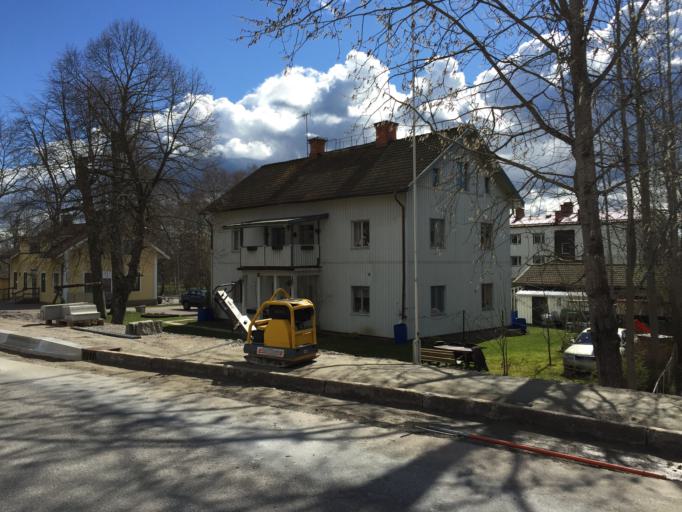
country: SE
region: OEstergoetland
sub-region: Norrkopings Kommun
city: Svartinge
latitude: 58.8290
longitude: 15.9328
